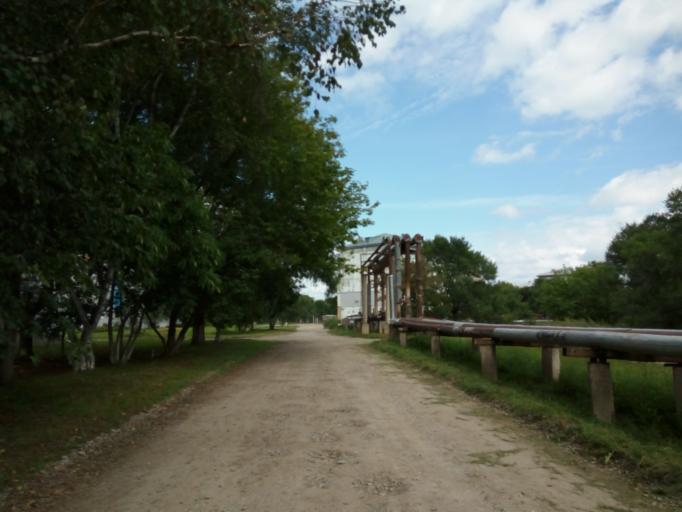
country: RU
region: Primorskiy
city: Dal'nerechensk
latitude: 45.9433
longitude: 133.8163
